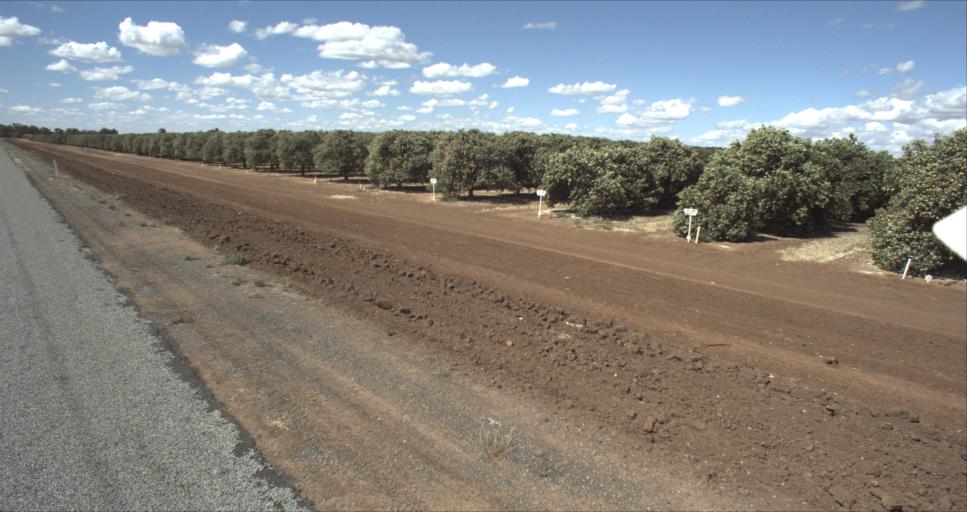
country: AU
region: New South Wales
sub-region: Leeton
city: Leeton
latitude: -34.5231
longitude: 146.2227
